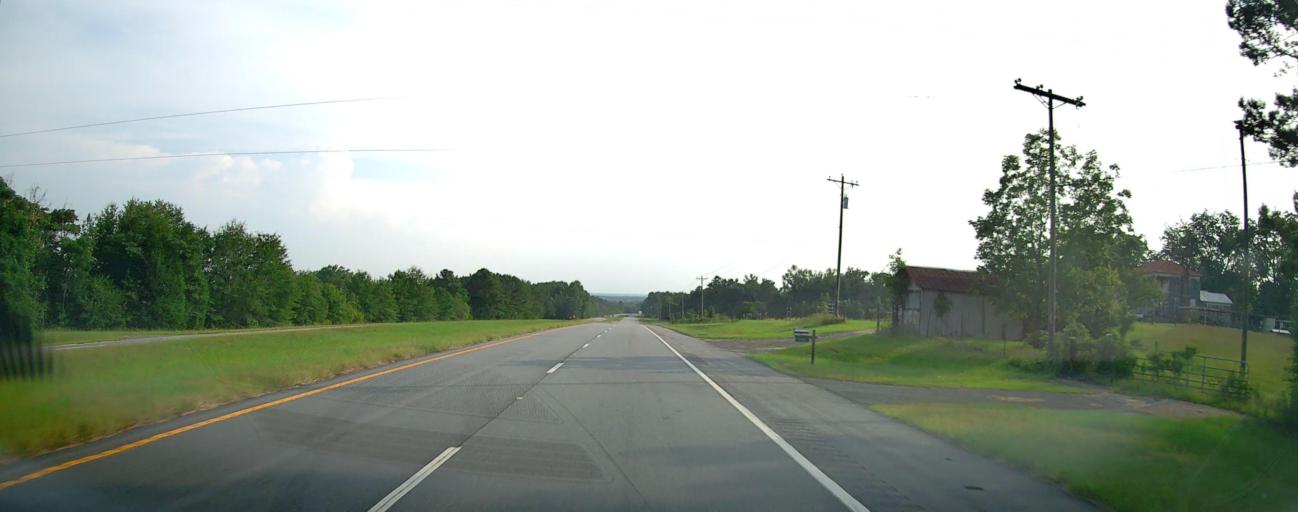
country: US
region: Georgia
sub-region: Talbot County
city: Talbotton
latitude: 32.5727
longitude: -84.5981
